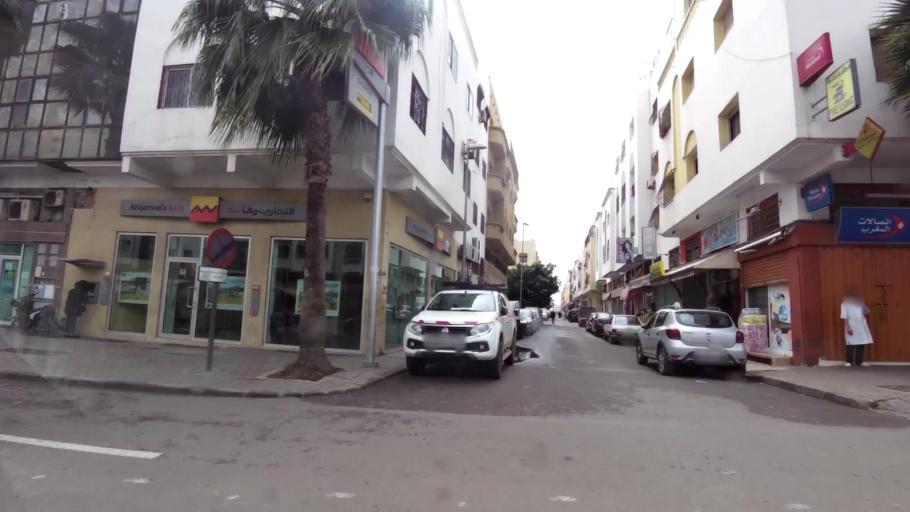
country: MA
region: Grand Casablanca
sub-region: Casablanca
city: Casablanca
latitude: 33.5402
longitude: -7.6828
